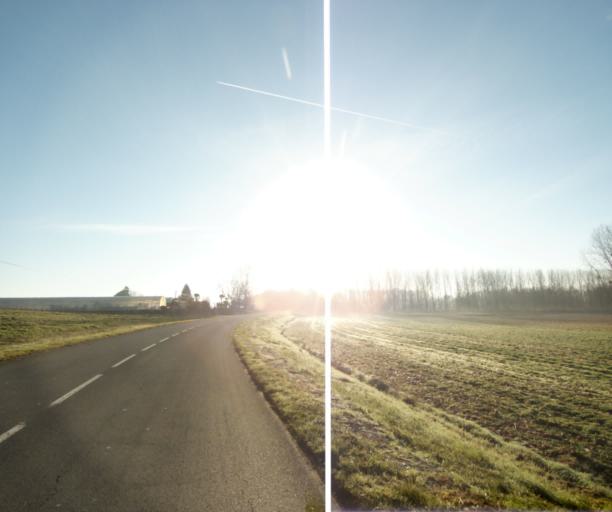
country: FR
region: Poitou-Charentes
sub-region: Departement de la Charente-Maritime
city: Cherac
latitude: 45.6961
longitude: -0.4802
